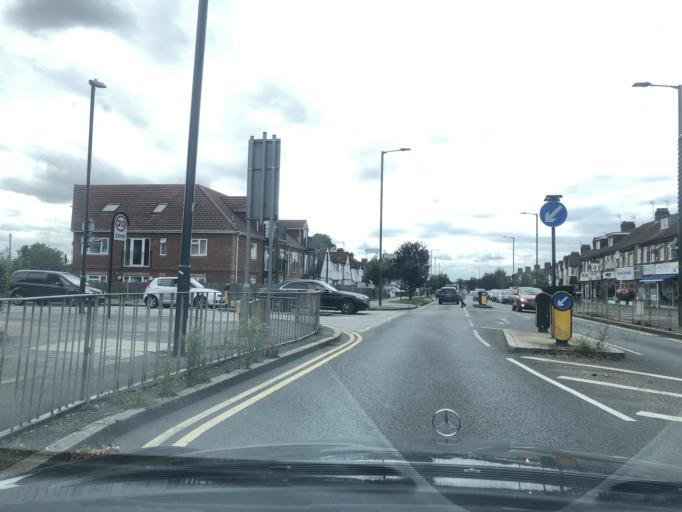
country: GB
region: England
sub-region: Greater London
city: Northolt
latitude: 51.5619
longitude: -0.3723
